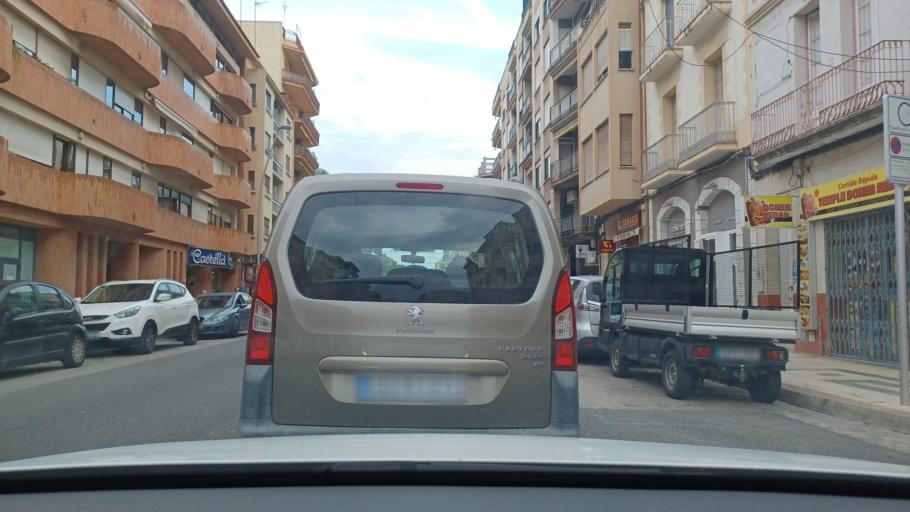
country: ES
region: Catalonia
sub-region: Provincia de Tarragona
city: Tortosa
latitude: 40.8060
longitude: 0.5204
